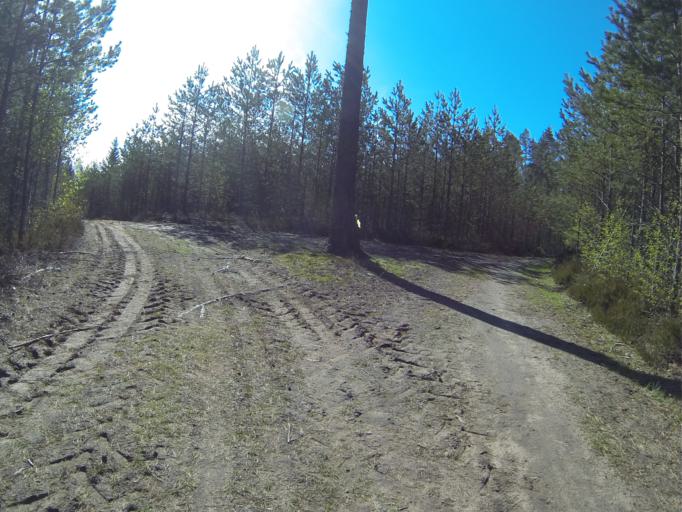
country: FI
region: Varsinais-Suomi
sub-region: Salo
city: Pertteli
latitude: 60.3917
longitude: 23.2152
